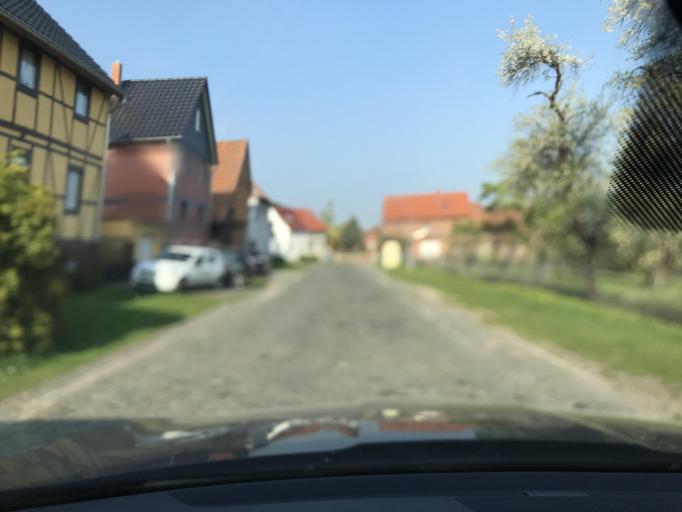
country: DE
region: Saxony-Anhalt
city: Huy-Neinstedt
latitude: 51.9738
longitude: 10.9848
